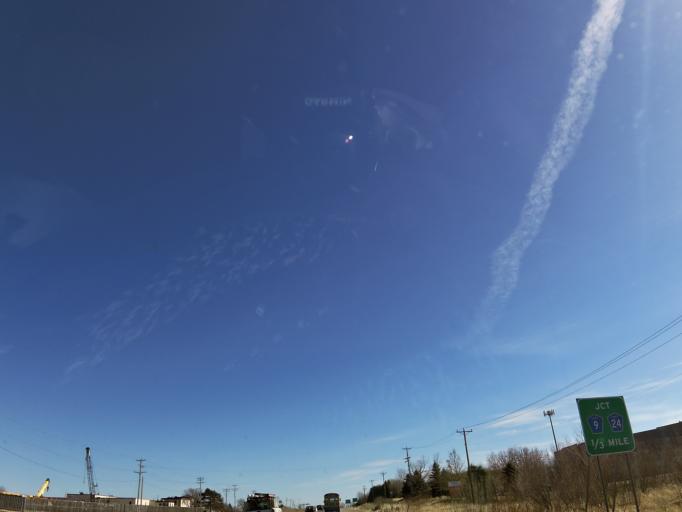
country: US
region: Minnesota
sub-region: Hennepin County
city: Plymouth
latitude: 45.0256
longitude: -93.4983
